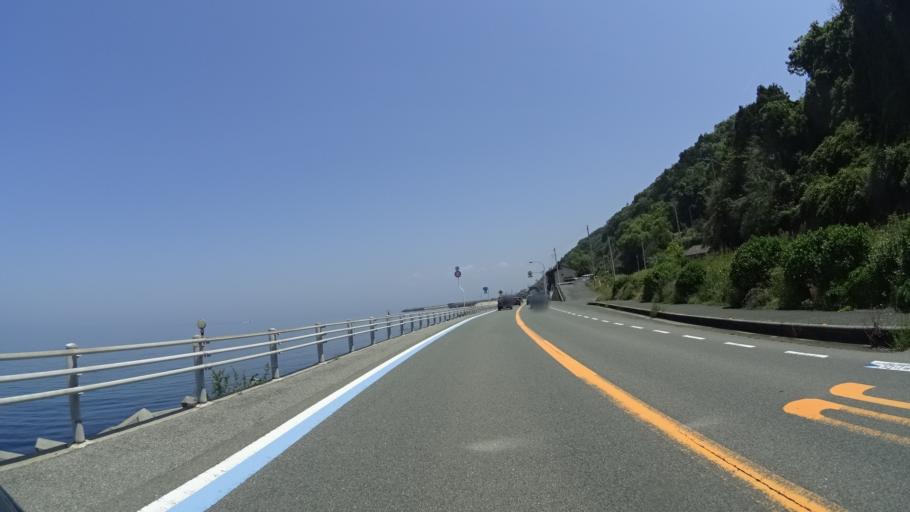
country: JP
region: Ehime
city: Ozu
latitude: 33.6306
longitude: 132.5181
